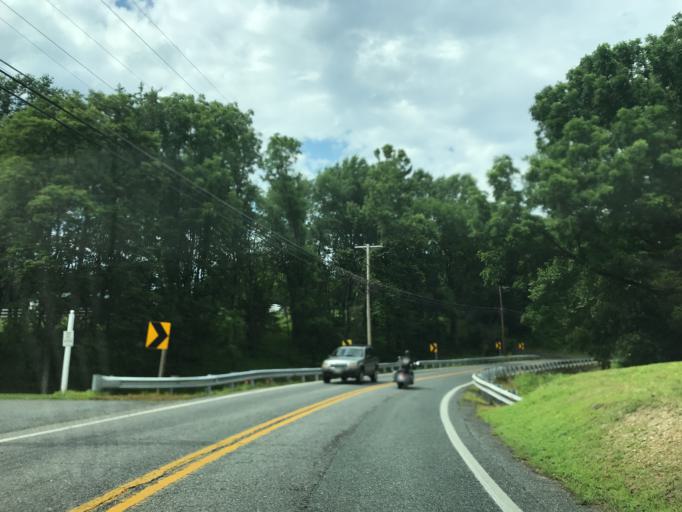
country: US
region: Maryland
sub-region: Harford County
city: Bel Air North
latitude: 39.6044
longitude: -76.3976
